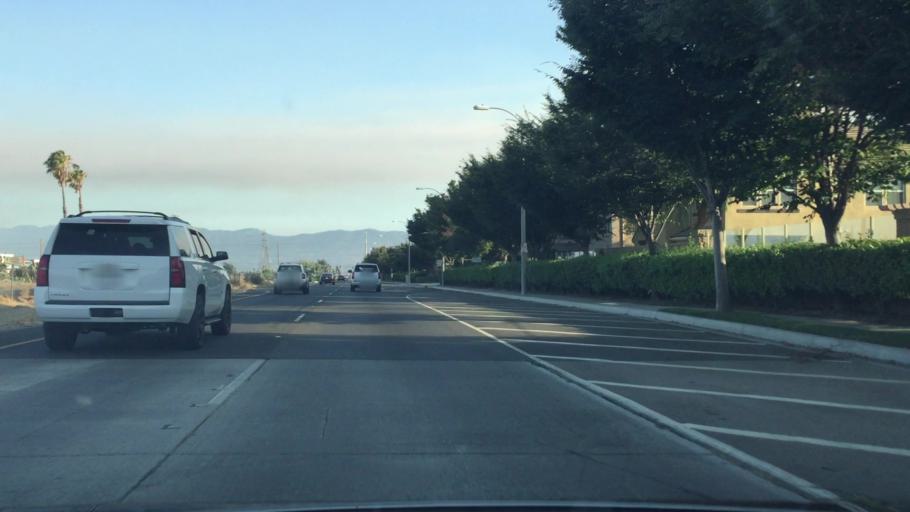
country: US
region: California
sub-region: San Bernardino County
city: Chino
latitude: 34.0095
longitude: -117.6510
